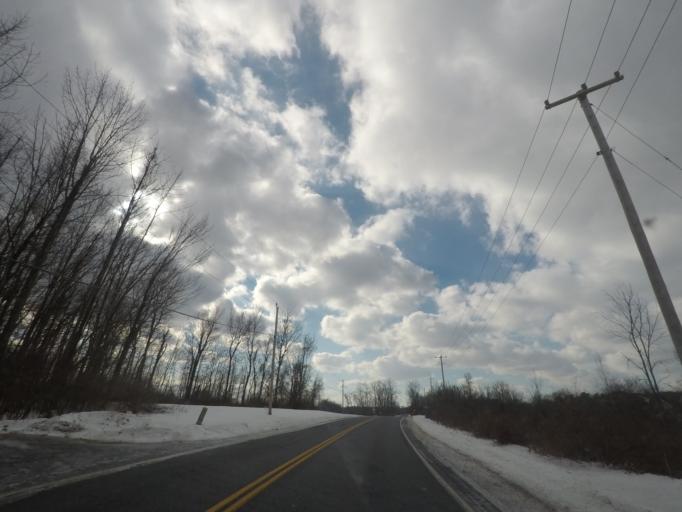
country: US
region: New York
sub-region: Saratoga County
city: Mechanicville
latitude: 42.8985
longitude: -73.7454
